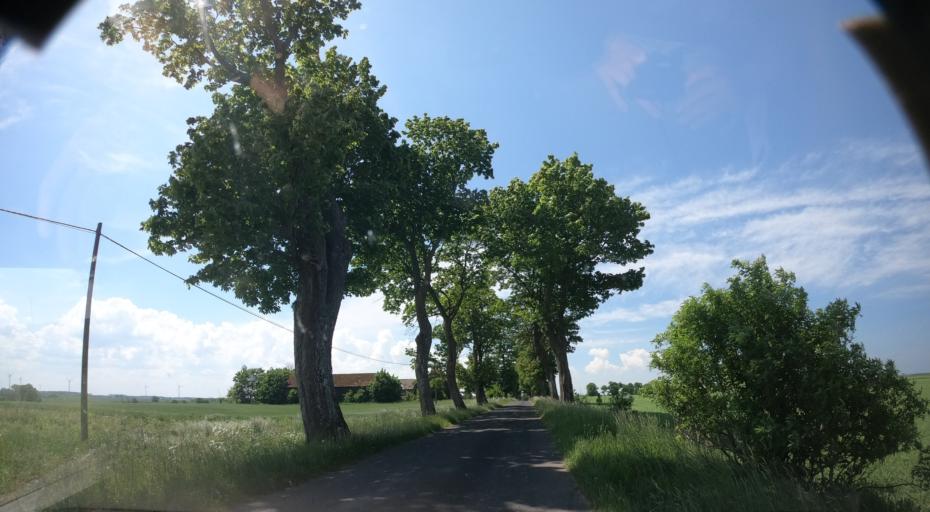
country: PL
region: West Pomeranian Voivodeship
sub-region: Powiat kolobrzeski
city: Ustronie Morskie
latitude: 54.1515
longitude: 15.7915
